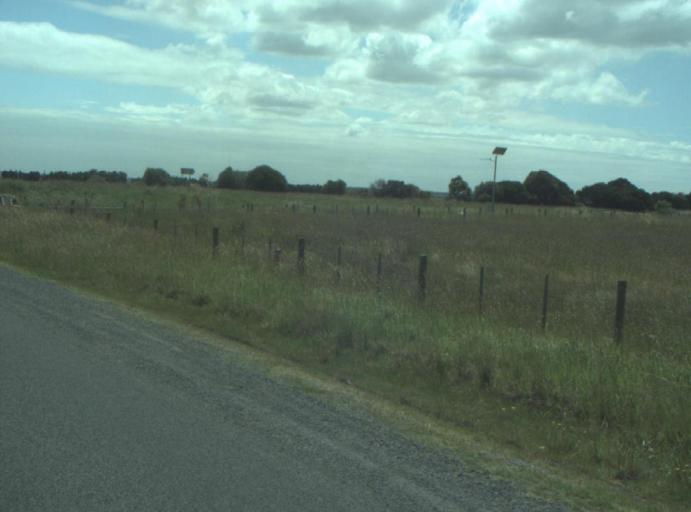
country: AU
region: Victoria
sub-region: Greater Geelong
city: Leopold
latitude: -38.2662
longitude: 144.4451
